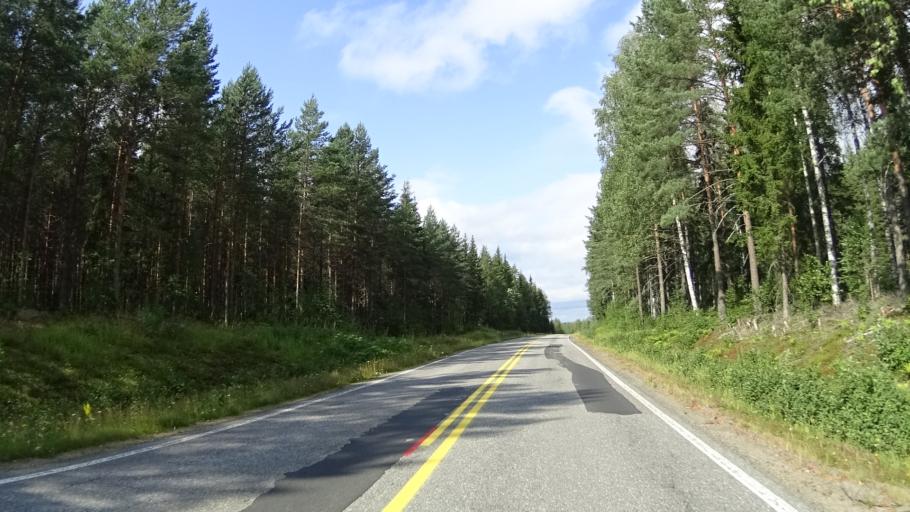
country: FI
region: Pirkanmaa
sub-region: Tampere
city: Luopioinen
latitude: 61.4811
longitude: 24.7430
